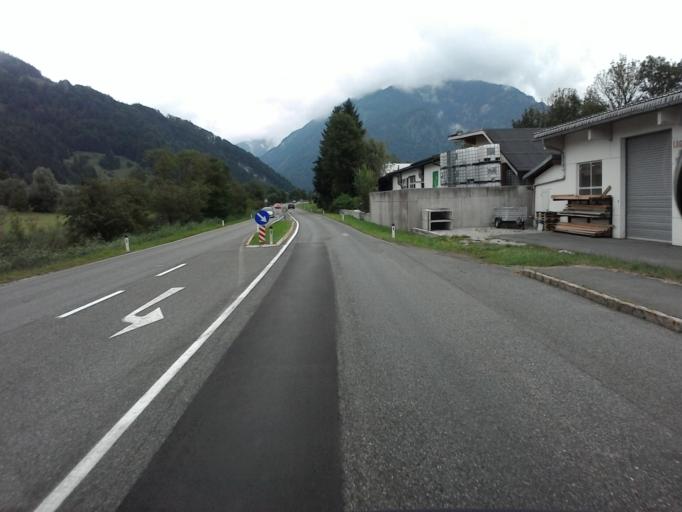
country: AT
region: Tyrol
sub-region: Politischer Bezirk Kitzbuhel
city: Kirchdorf in Tirol
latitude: 47.5664
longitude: 12.4675
